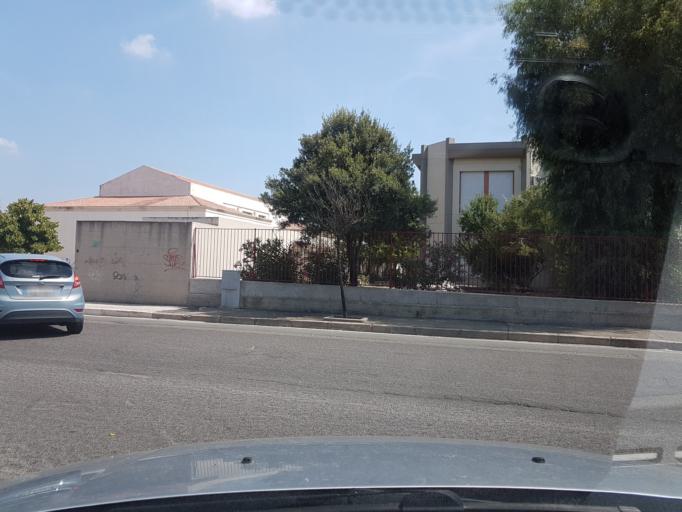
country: IT
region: Sardinia
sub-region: Provincia di Oristano
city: Oristano
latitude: 39.9068
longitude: 8.5999
